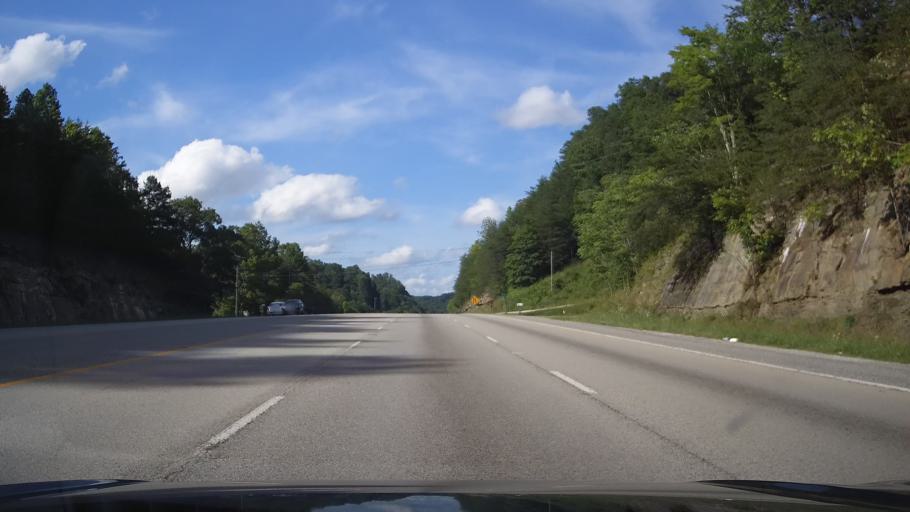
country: US
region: Kentucky
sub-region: Lawrence County
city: Louisa
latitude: 38.0363
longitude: -82.6507
